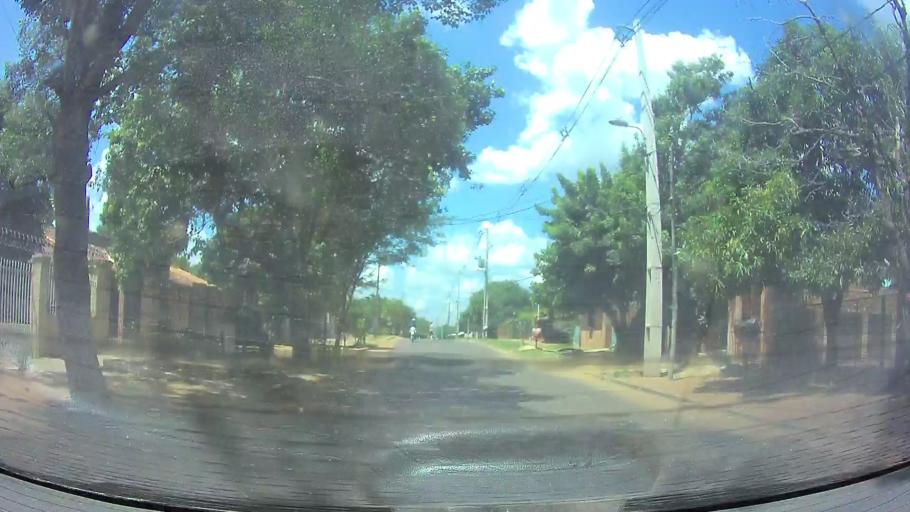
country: PY
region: Central
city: Limpio
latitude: -25.1520
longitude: -57.4555
